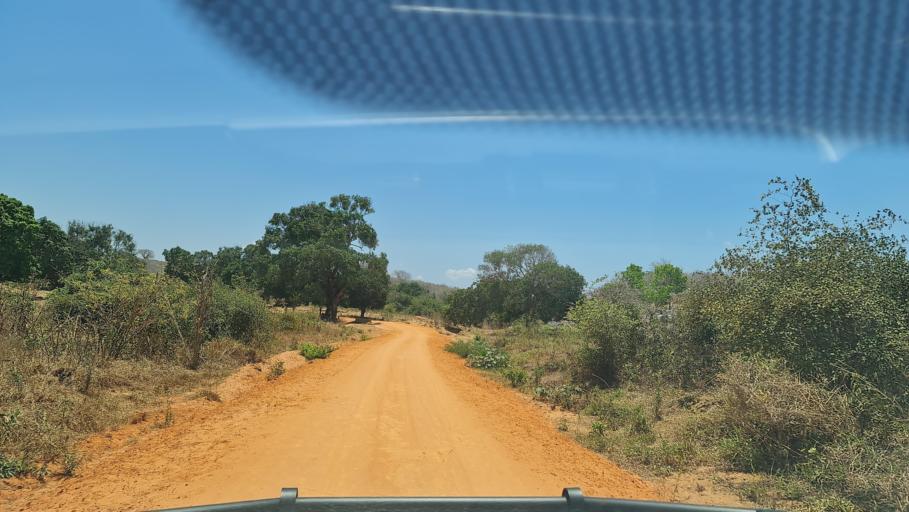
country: MZ
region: Nampula
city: Nacala
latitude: -14.2111
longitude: 40.6776
